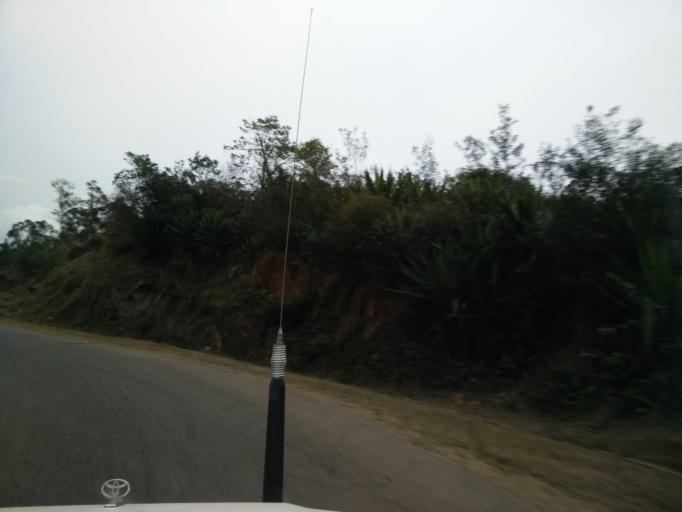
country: MG
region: Upper Matsiatra
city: Fianarantsoa
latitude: -21.5773
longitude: 47.0362
